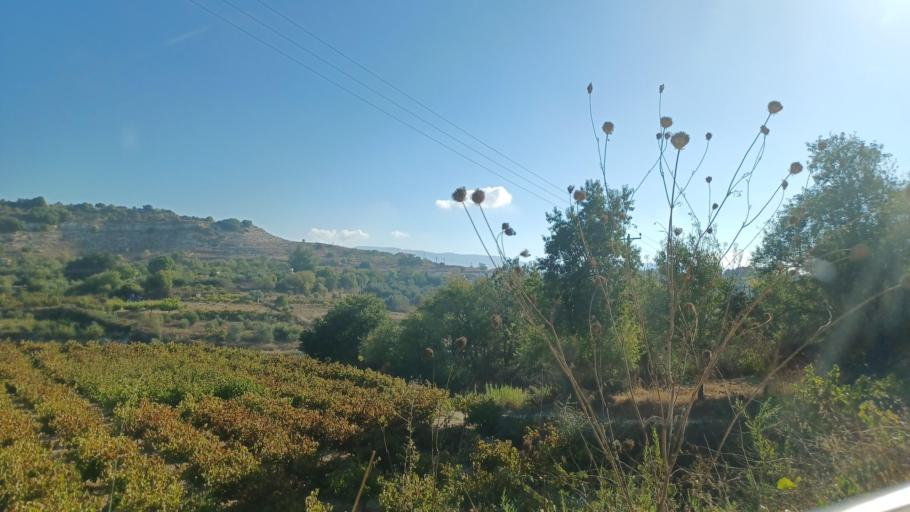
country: CY
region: Pafos
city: Mesogi
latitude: 34.8512
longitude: 32.5154
